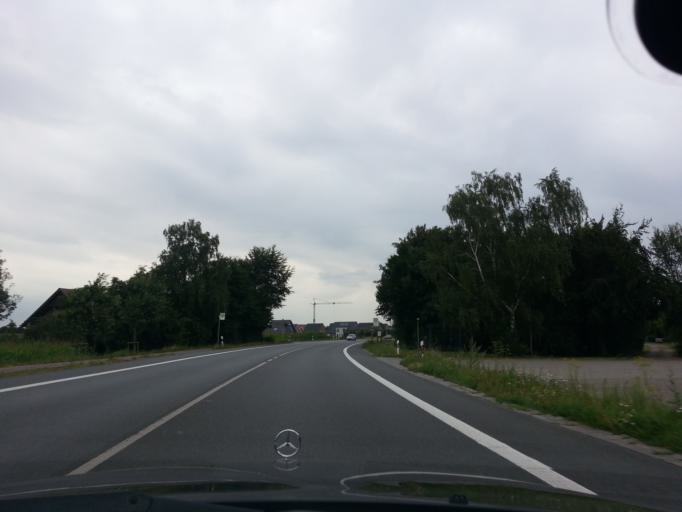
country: DE
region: North Rhine-Westphalia
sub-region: Regierungsbezirk Munster
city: Raesfeld
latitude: 51.7623
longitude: 6.8529
